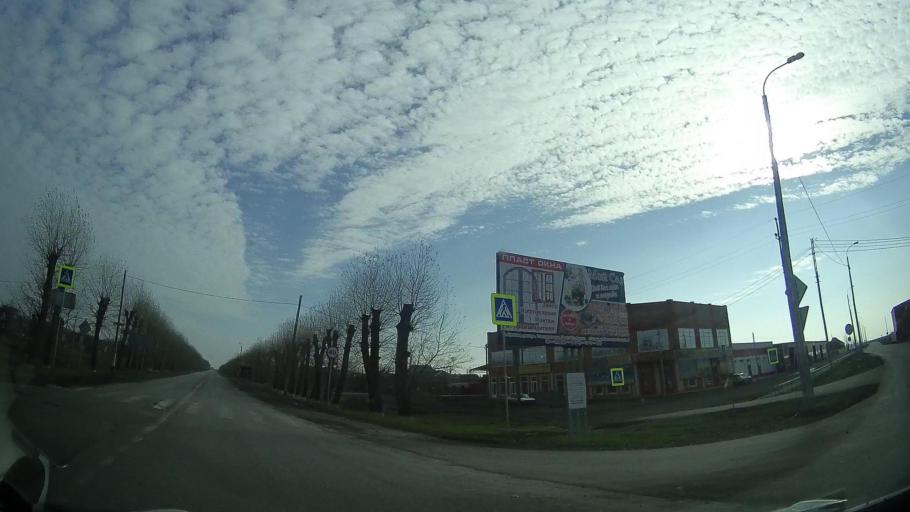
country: RU
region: Rostov
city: Tselina
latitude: 46.5290
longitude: 41.0525
